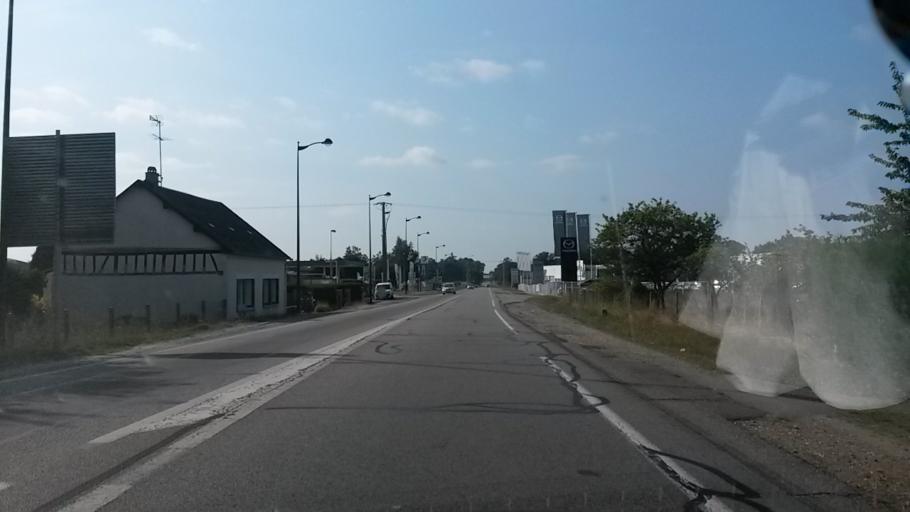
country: FR
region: Haute-Normandie
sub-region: Departement de l'Eure
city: Evreux
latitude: 48.9969
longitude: 1.1553
